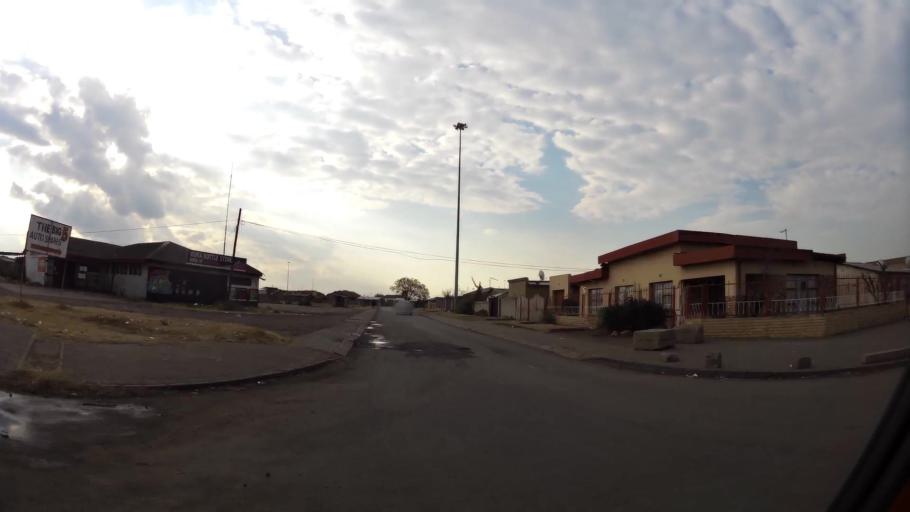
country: ZA
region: Gauteng
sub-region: Sedibeng District Municipality
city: Vanderbijlpark
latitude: -26.6968
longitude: 27.8752
